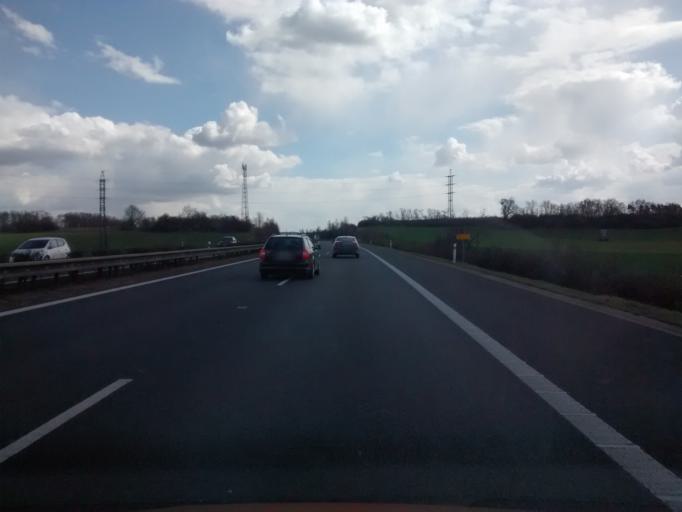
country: CZ
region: Central Bohemia
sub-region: Okres Melnik
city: Veltrusy
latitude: 50.2742
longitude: 14.3565
